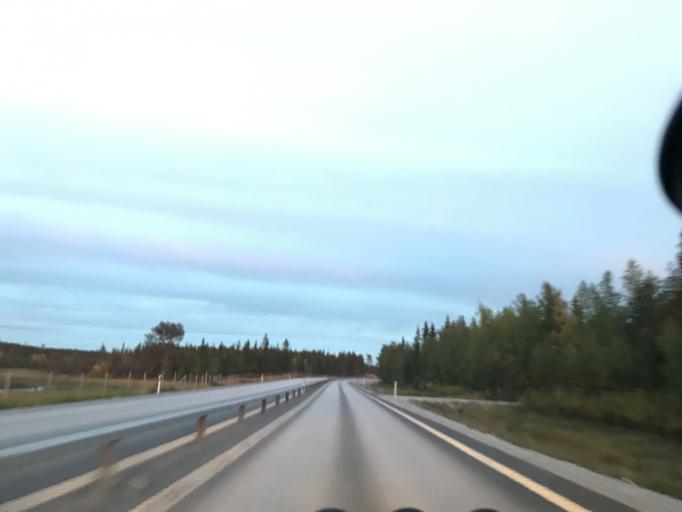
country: SE
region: Norrbotten
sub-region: Gallivare Kommun
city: Malmberget
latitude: 67.6601
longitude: 21.0004
